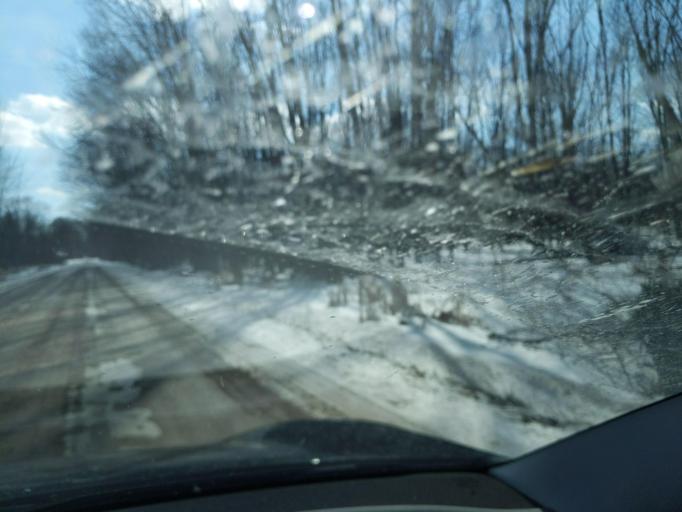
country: US
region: Michigan
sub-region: Livingston County
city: Fowlerville
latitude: 42.5549
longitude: -84.0885
